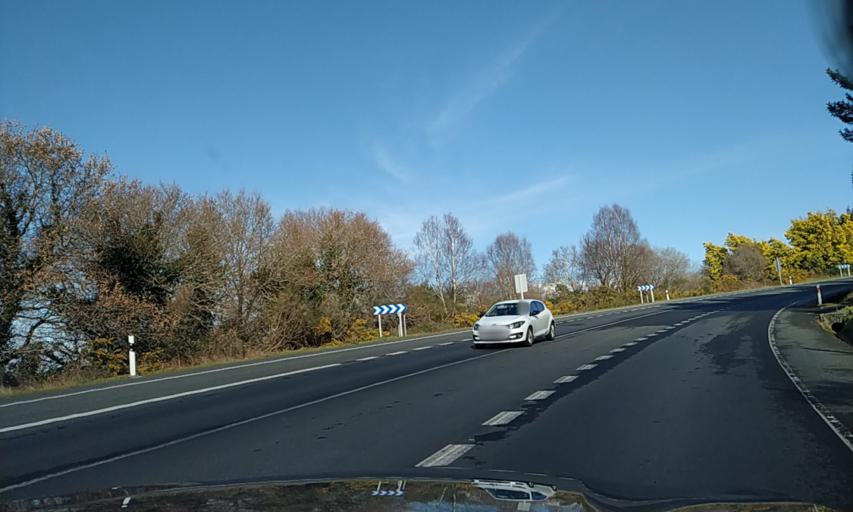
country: ES
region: Galicia
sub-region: Provincia da Coruna
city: Ribeira
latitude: 42.7143
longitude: -8.3752
